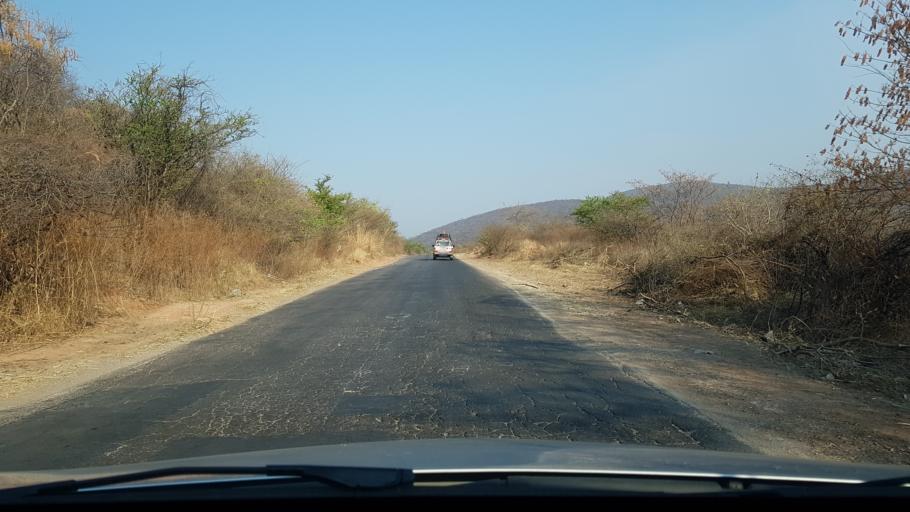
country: MX
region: Morelos
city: Tlaltizapan
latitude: 18.6715
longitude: -99.0560
